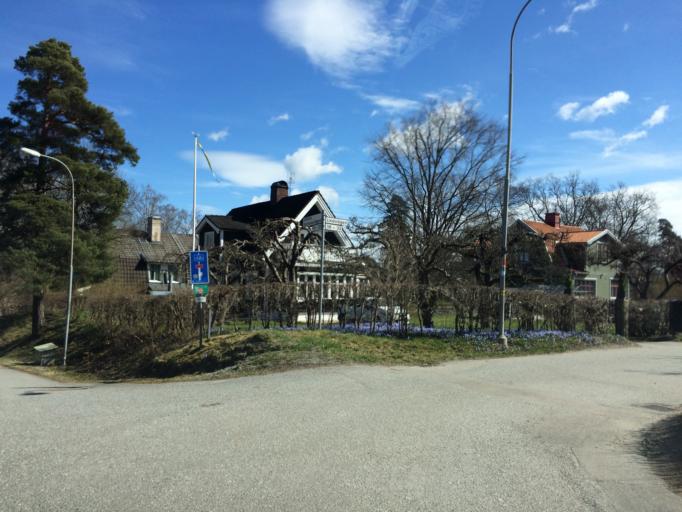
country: SE
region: Stockholm
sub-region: Sollentuna Kommun
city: Sollentuna
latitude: 59.4580
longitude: 17.9197
